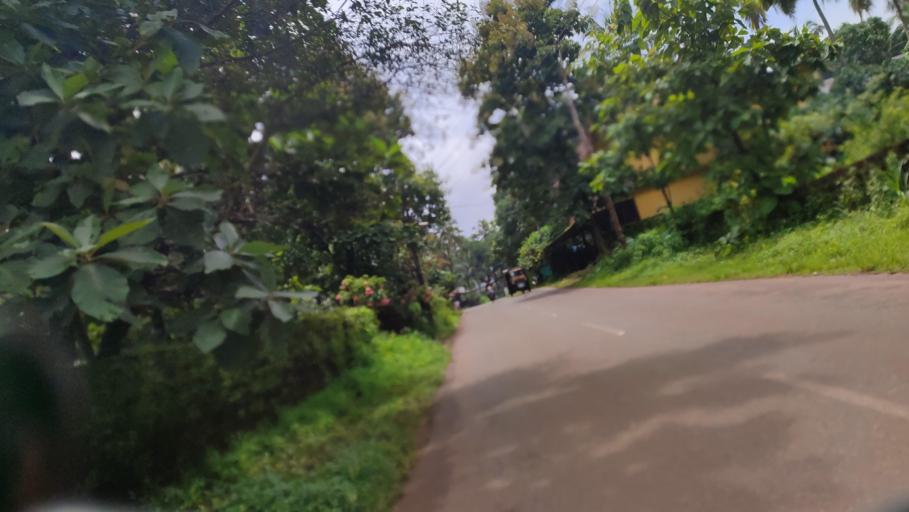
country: IN
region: Kerala
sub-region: Kasaragod District
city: Kannangad
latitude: 12.3921
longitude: 75.0449
